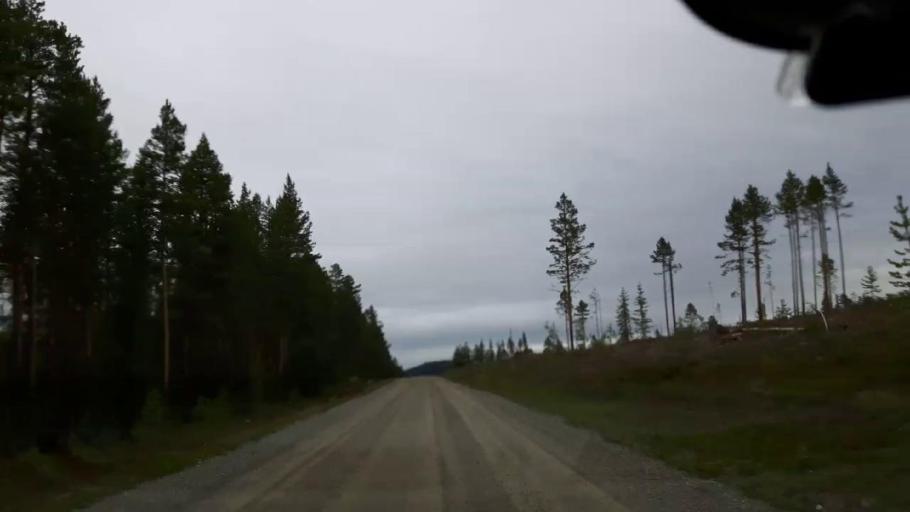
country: SE
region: Vaesternorrland
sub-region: Ange Kommun
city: Fransta
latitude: 62.8596
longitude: 16.0414
